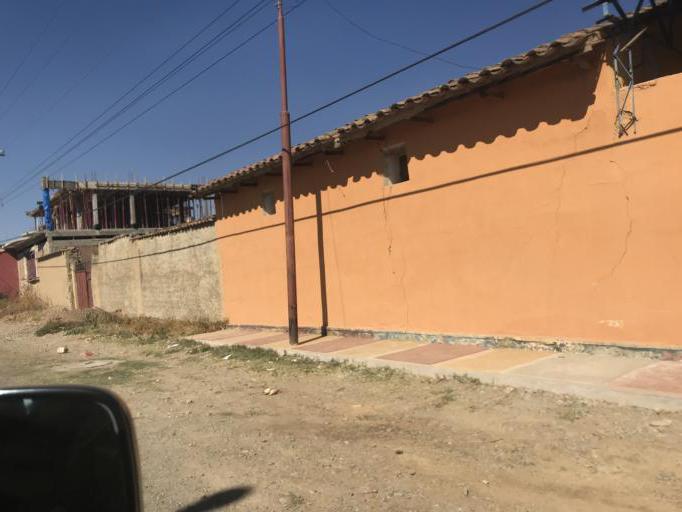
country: BO
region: Cochabamba
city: Punata
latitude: -17.5641
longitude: -65.8838
